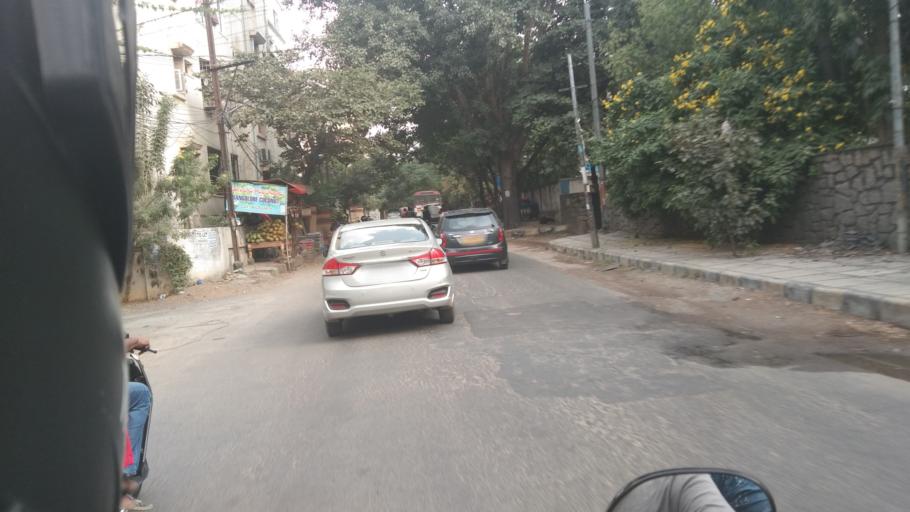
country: IN
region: Telangana
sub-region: Rangareddi
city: Kukatpalli
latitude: 17.4312
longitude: 78.4227
